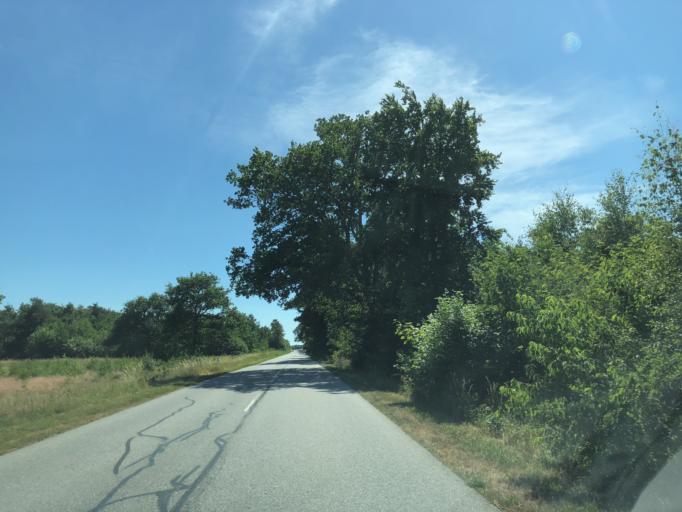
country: DK
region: Central Jutland
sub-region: Skive Kommune
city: Skive
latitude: 56.5113
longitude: 9.0231
